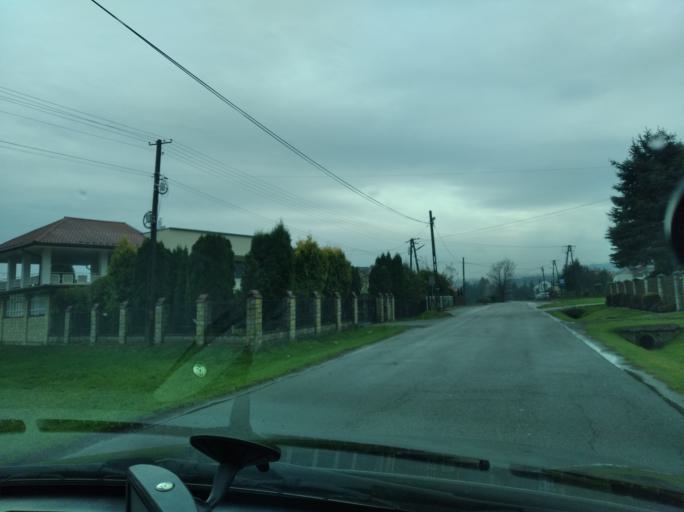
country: PL
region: Subcarpathian Voivodeship
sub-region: Powiat strzyzowski
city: Czudec
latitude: 49.9347
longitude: 21.8459
